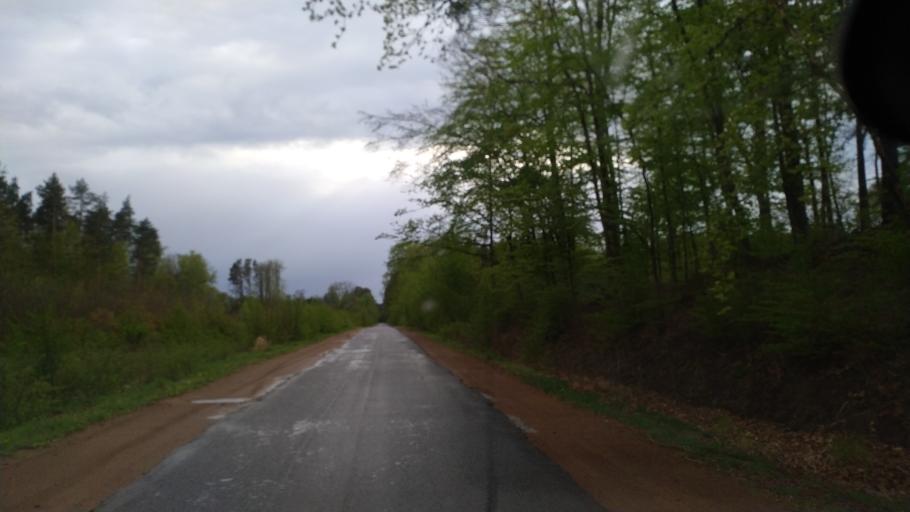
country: PL
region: Pomeranian Voivodeship
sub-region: Powiat starogardzki
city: Osiek
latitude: 53.7089
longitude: 18.5841
